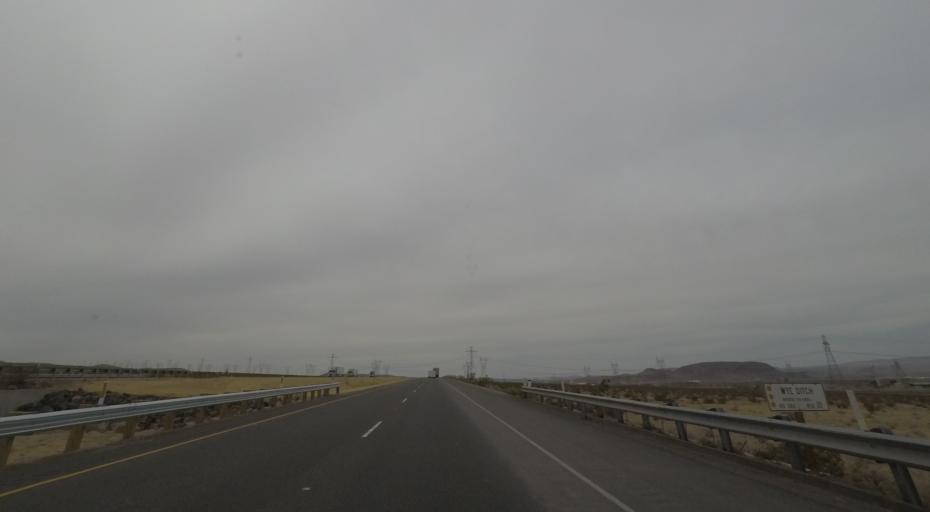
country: US
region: California
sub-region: San Bernardino County
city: Barstow
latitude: 34.8455
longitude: -116.8353
